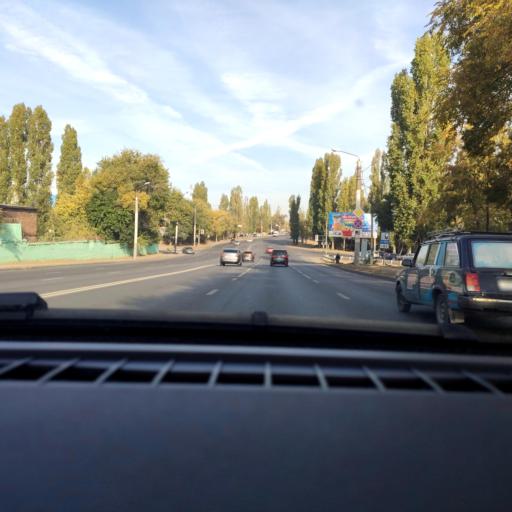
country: RU
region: Voronezj
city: Maslovka
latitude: 51.6230
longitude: 39.2343
